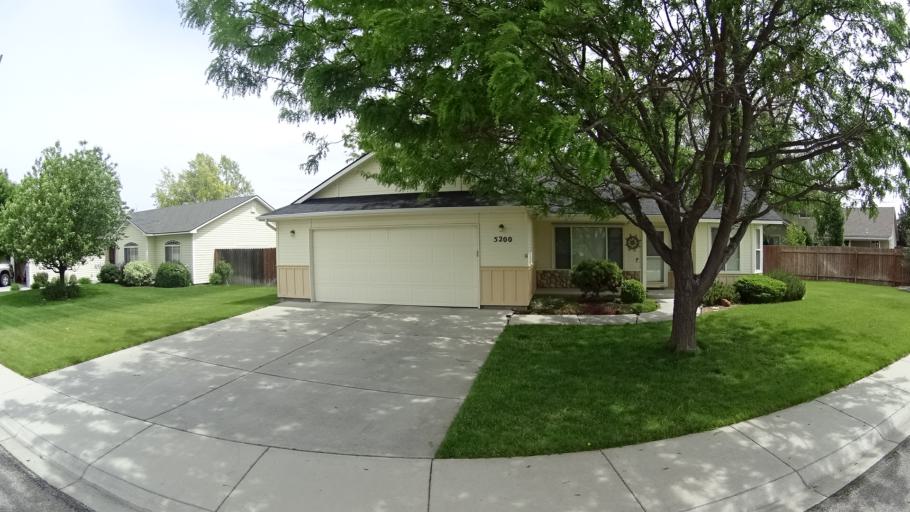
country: US
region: Idaho
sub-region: Ada County
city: Meridian
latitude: 43.5555
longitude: -116.3370
